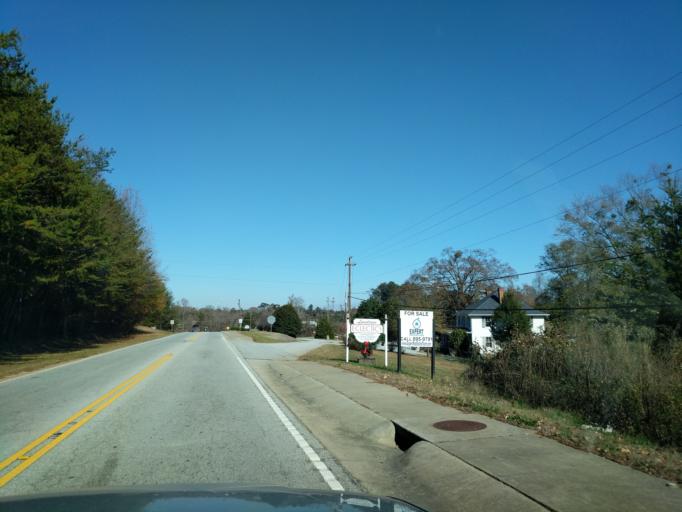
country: US
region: South Carolina
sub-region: Spartanburg County
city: Landrum
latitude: 35.1657
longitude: -82.1974
